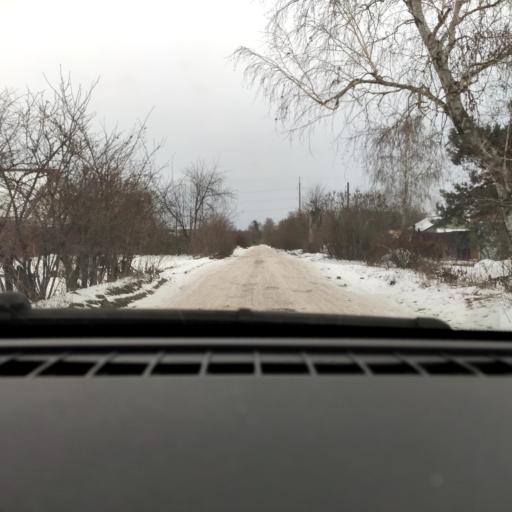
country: RU
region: Voronezj
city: Maslovka
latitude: 51.6026
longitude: 39.2822
